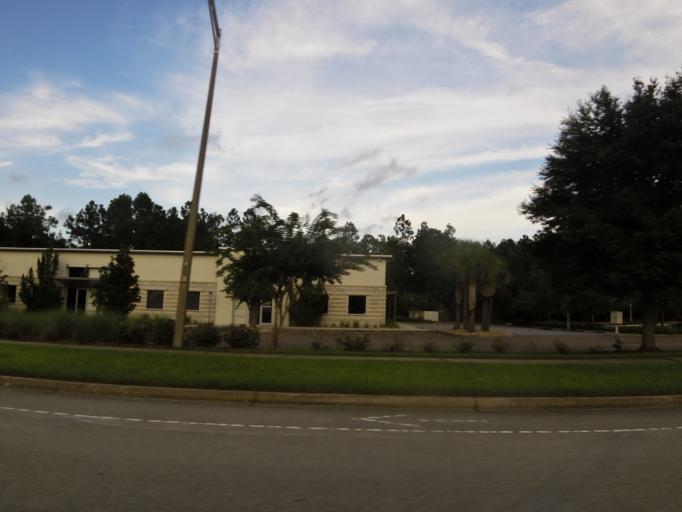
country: US
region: Florida
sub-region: Saint Johns County
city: Ponte Vedra Beach
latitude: 30.2349
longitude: -81.5103
